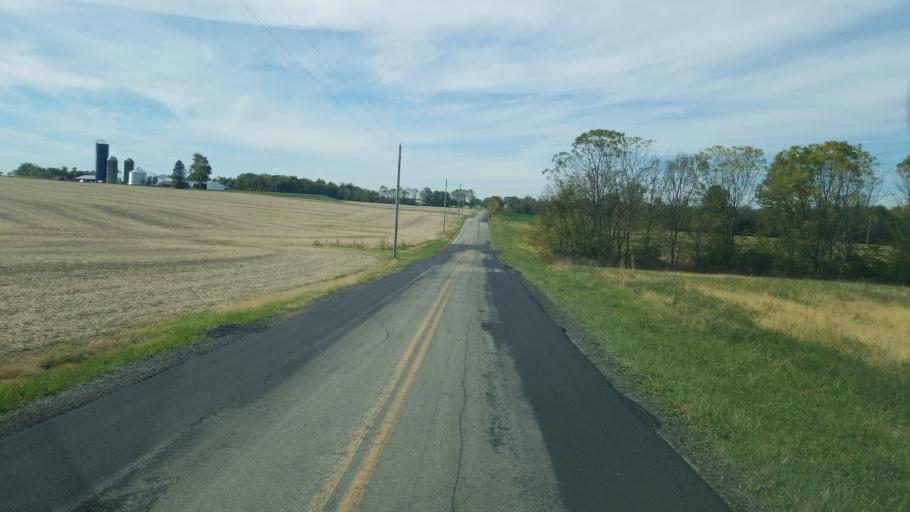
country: US
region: Ohio
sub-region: Highland County
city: Leesburg
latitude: 39.3281
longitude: -83.4848
